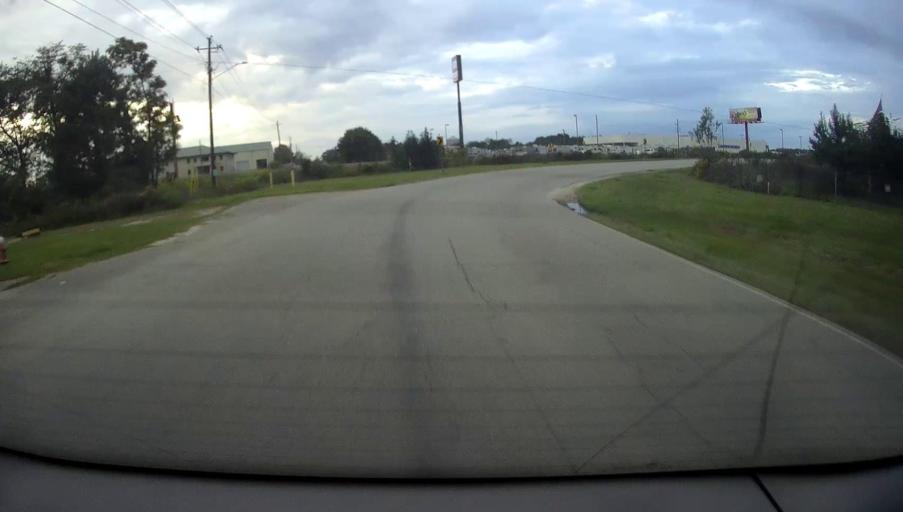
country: US
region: Georgia
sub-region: Peach County
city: Byron
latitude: 32.6511
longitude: -83.7426
